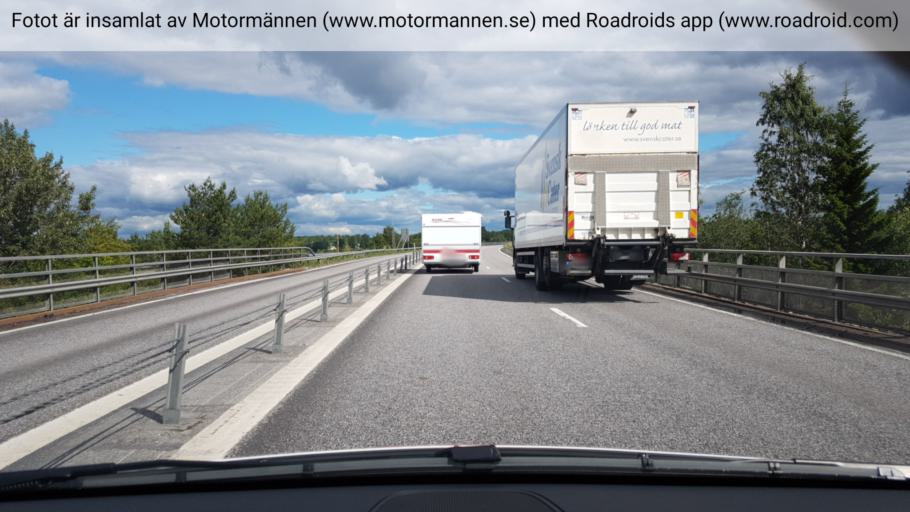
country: SE
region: Norrbotten
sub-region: Pitea Kommun
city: Bergsviken
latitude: 65.3113
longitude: 21.4081
